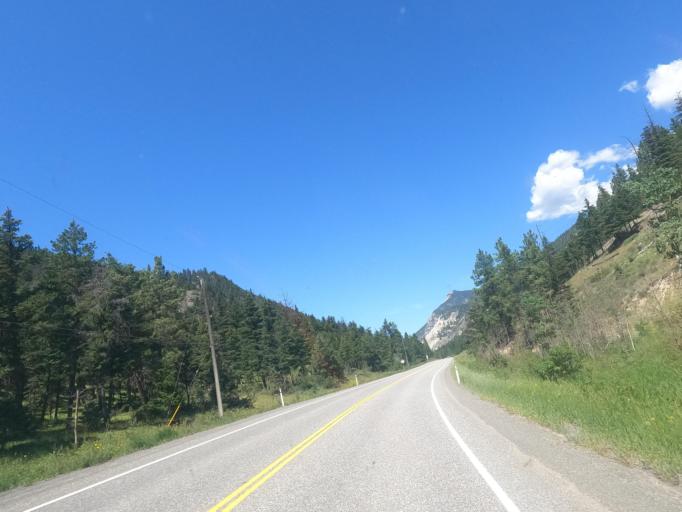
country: CA
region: British Columbia
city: Cache Creek
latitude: 50.7998
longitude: -121.6211
